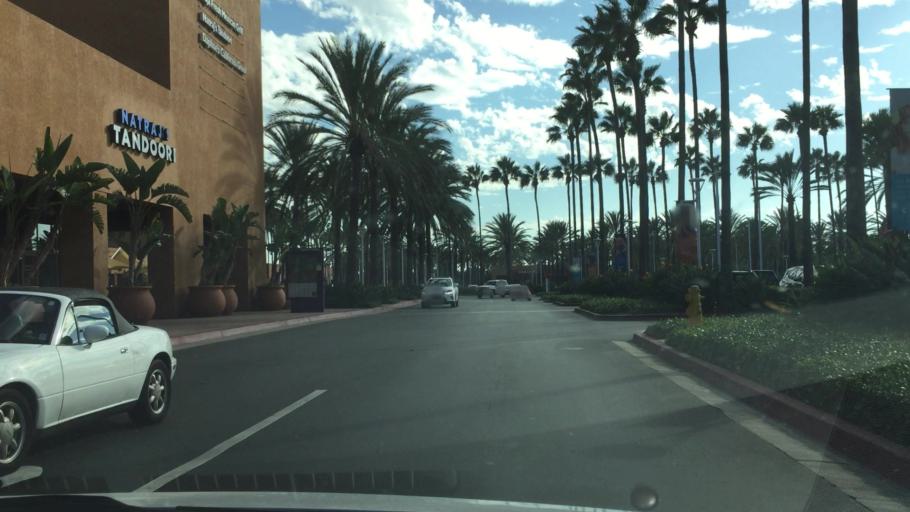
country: US
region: California
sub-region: Orange County
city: North Tustin
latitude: 33.7284
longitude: -117.7865
